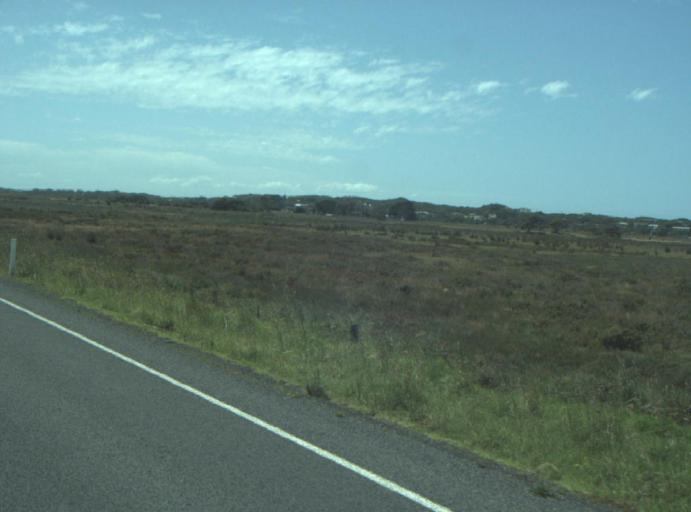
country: AU
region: Victoria
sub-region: Greater Geelong
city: Breakwater
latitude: -38.2919
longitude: 144.3771
